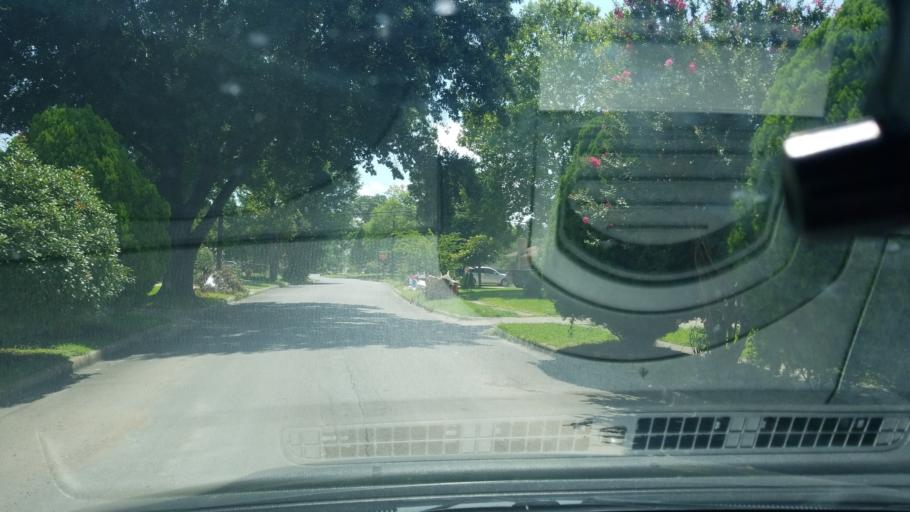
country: US
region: Texas
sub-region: Dallas County
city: Balch Springs
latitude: 32.7463
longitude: -96.6877
